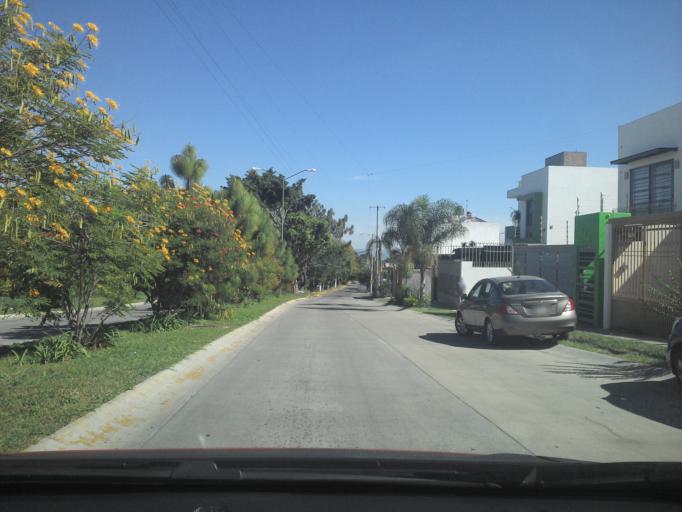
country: MX
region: Jalisco
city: Zapopan2
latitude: 20.7481
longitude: -103.4096
